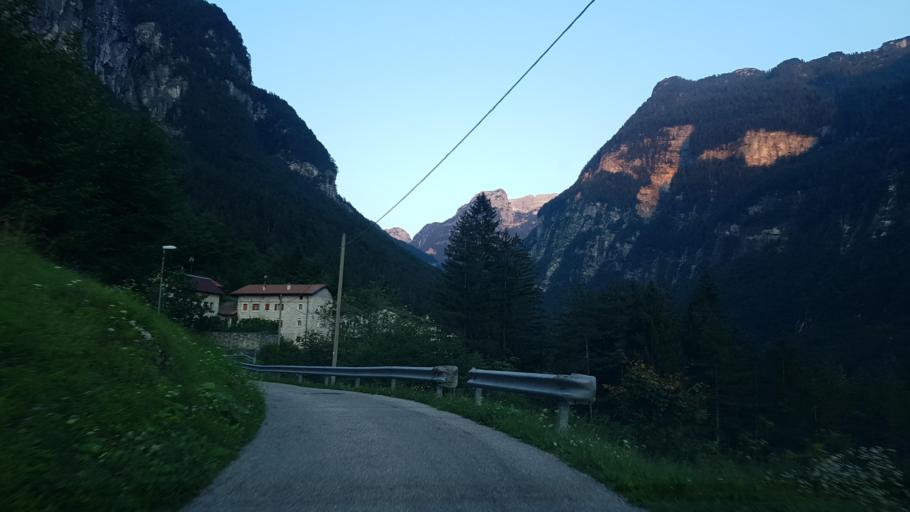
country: IT
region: Friuli Venezia Giulia
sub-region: Provincia di Udine
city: Malborghetto
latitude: 46.4014
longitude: 13.4231
